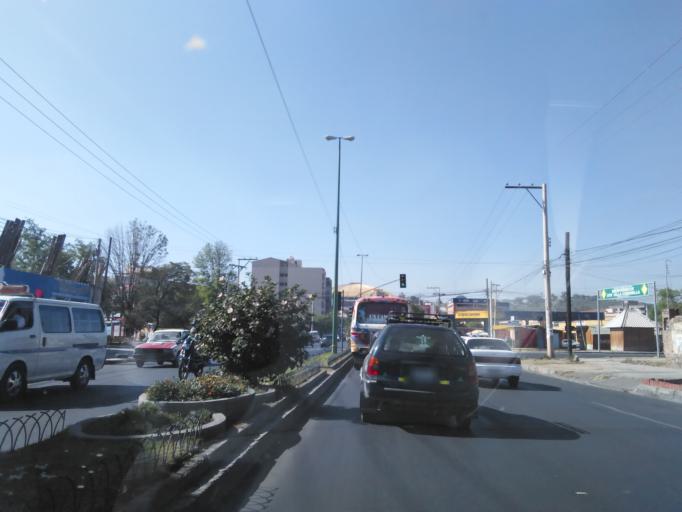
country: BO
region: Cochabamba
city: Cochabamba
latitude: -17.3982
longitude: -66.1655
